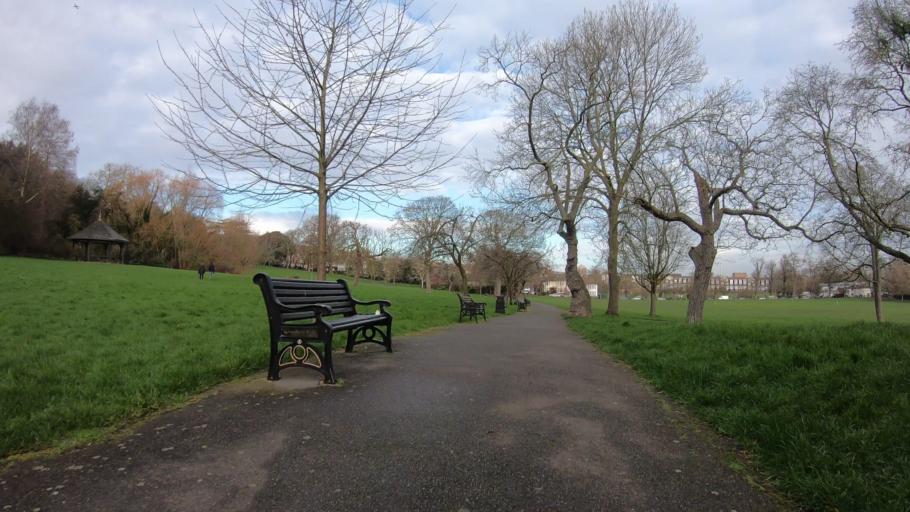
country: GB
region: England
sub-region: Greater London
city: Hackney
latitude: 51.5657
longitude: -0.0477
